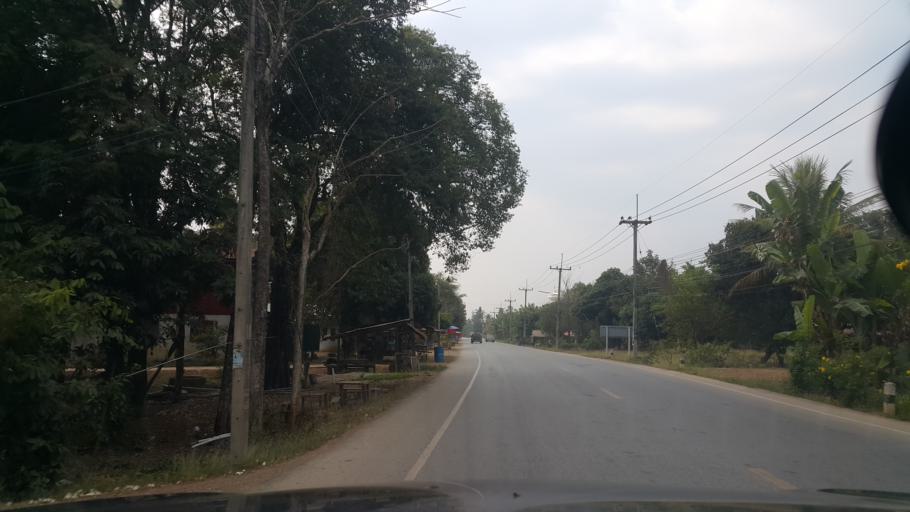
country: TH
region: Sukhothai
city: Si Samrong
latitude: 17.0852
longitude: 99.8823
